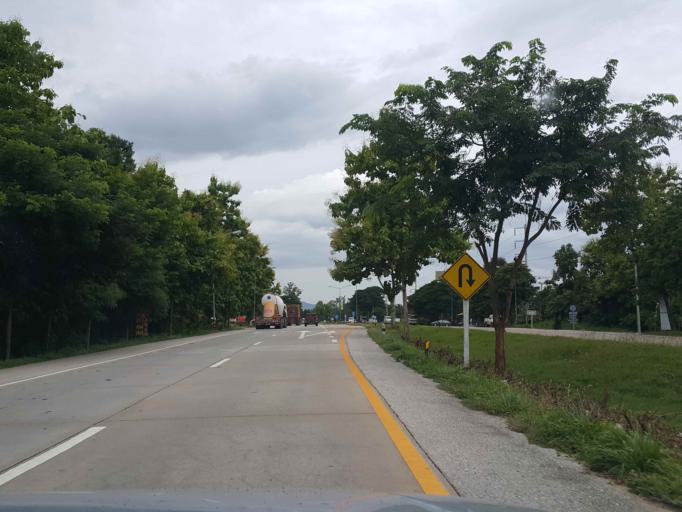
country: TH
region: Lampang
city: Hang Chat
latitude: 18.2977
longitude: 99.4128
